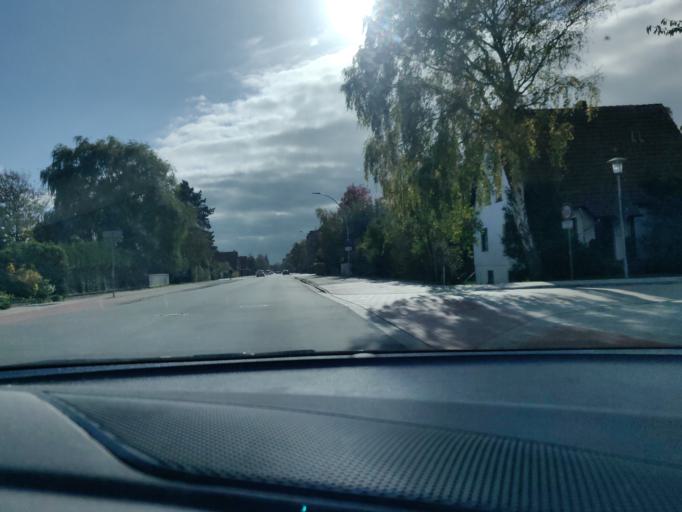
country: DE
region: Lower Saxony
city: Cuxhaven
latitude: 53.8584
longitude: 8.6876
